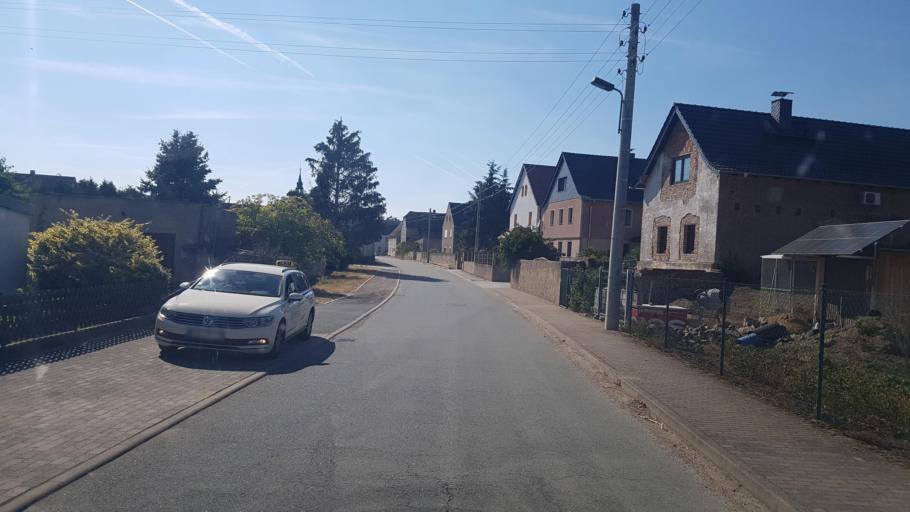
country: DE
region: Saxony
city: Strehla
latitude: 51.3803
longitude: 13.2841
